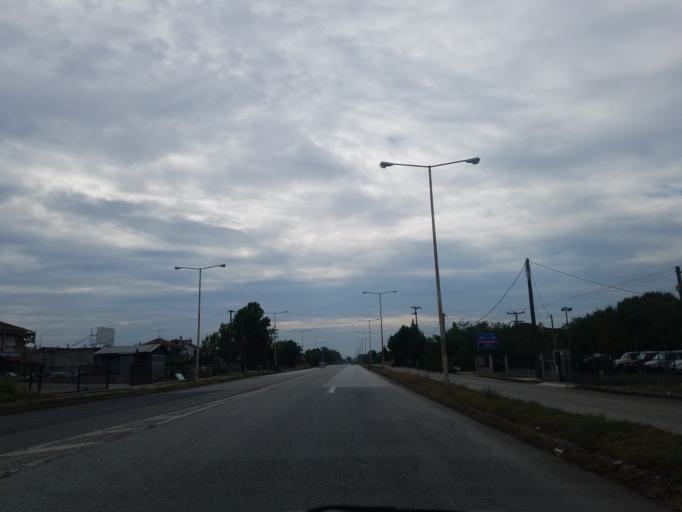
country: GR
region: Thessaly
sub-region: Trikala
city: Pyrgetos
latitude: 39.5836
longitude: 21.7399
